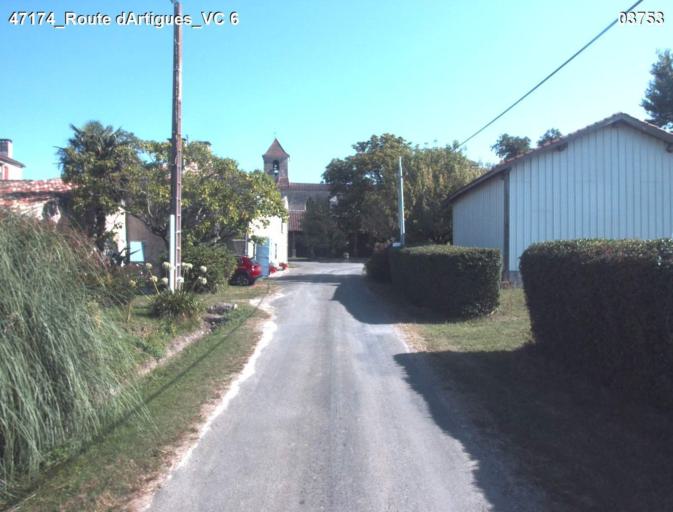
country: FR
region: Aquitaine
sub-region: Departement du Lot-et-Garonne
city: Mezin
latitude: 44.0398
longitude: 0.3382
